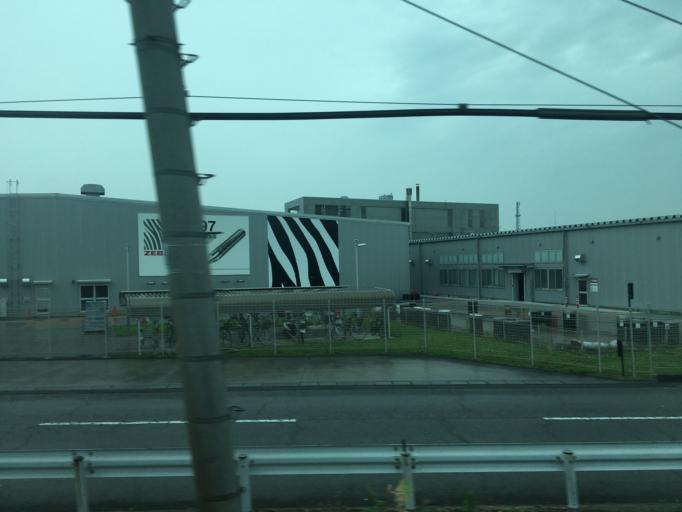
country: JP
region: Ibaraki
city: Koga
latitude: 36.2153
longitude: 139.7214
